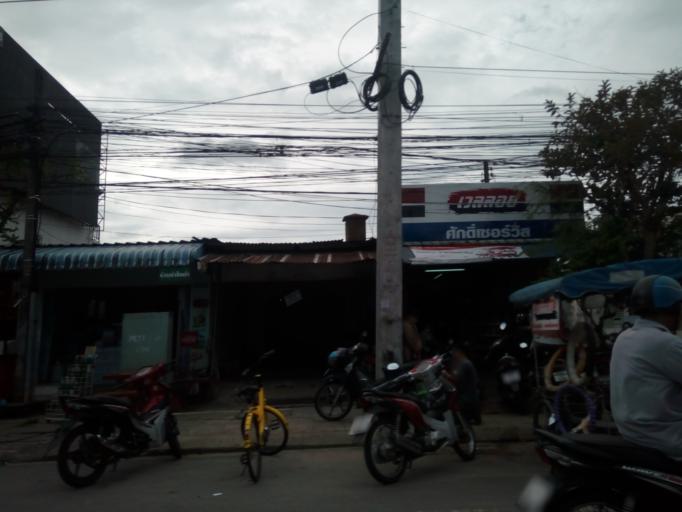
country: TH
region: Phuket
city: Mueang Phuket
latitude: 7.8596
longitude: 98.3803
